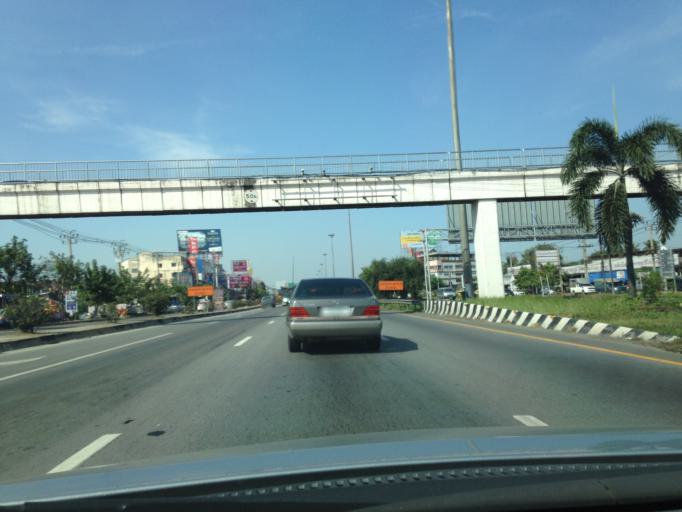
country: TH
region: Nonthaburi
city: Bang Yai
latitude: 13.8446
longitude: 100.4127
